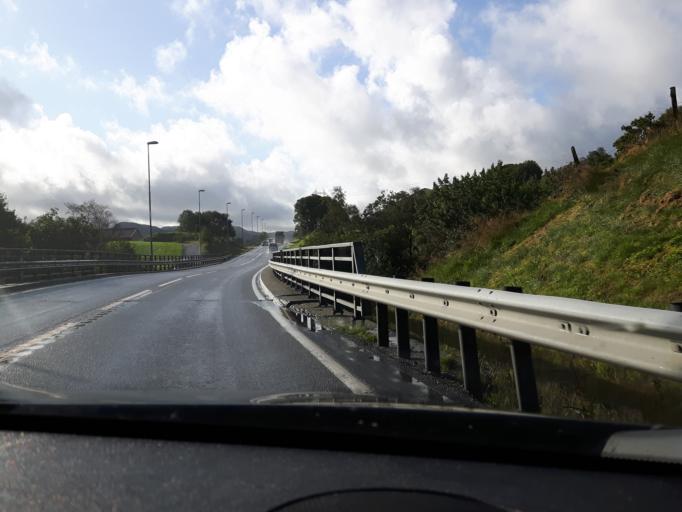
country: NO
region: Rogaland
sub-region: Gjesdal
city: Algard
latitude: 58.7272
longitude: 5.9686
